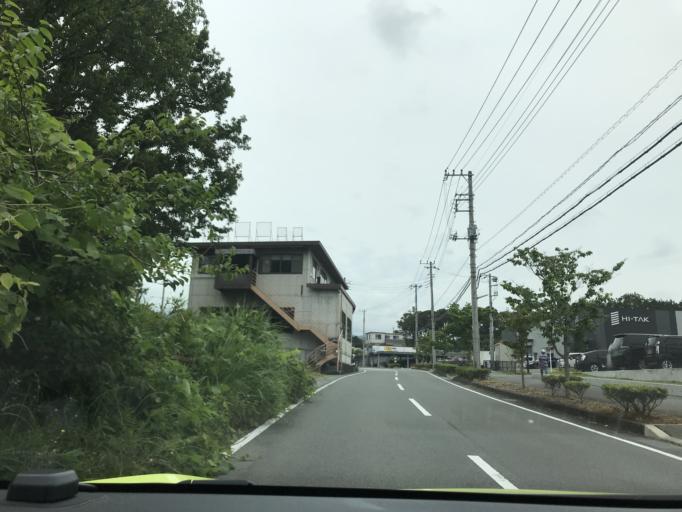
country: JP
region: Shizuoka
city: Numazu
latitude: 35.1360
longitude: 138.8578
